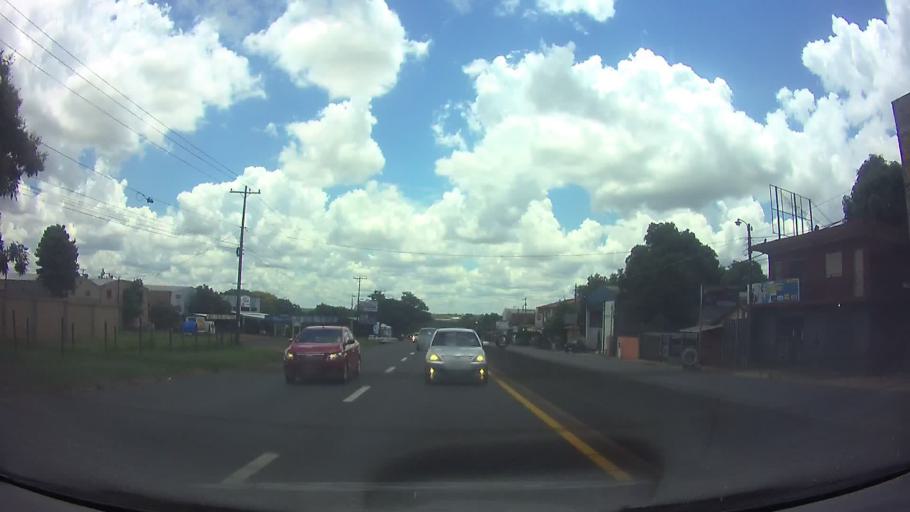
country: PY
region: Central
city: Capiata
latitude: -25.3784
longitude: -57.3917
